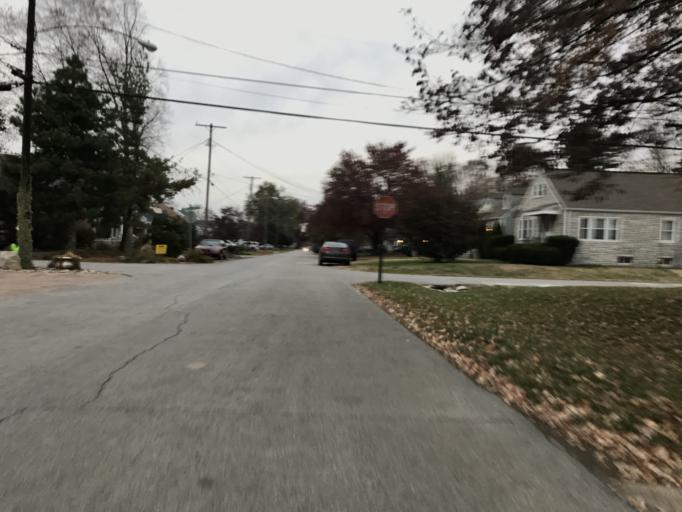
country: US
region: Kentucky
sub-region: Jefferson County
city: Audubon Park
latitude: 38.2128
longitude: -85.7353
